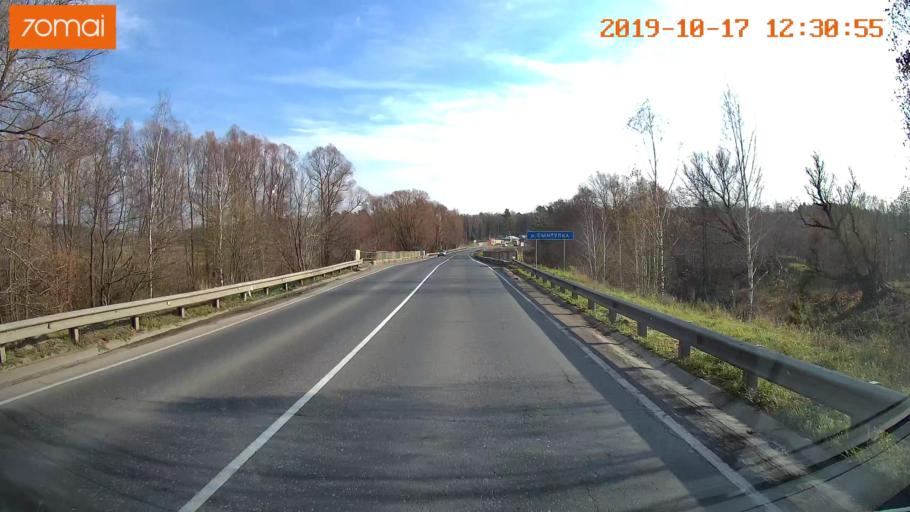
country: RU
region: Rjazan
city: Syntul
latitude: 54.9720
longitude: 41.3260
